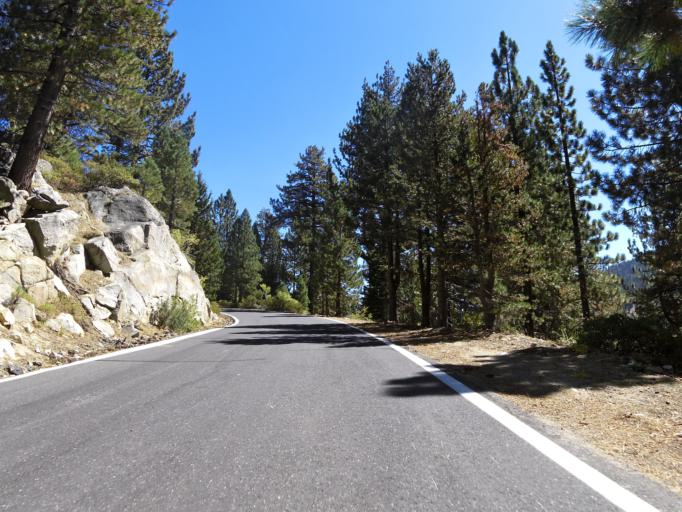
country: US
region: Nevada
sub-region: Douglas County
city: Gardnerville Ranchos
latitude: 38.5483
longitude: -119.8635
